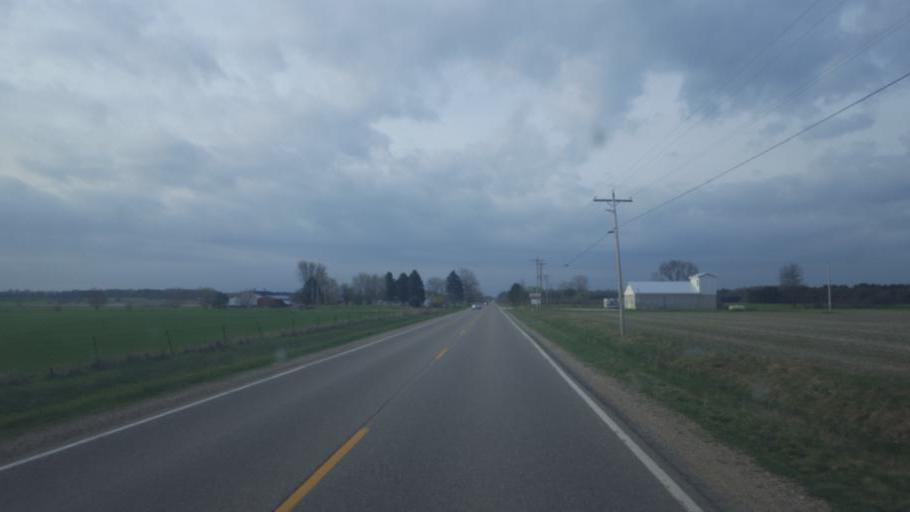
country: US
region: Michigan
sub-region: Isabella County
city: Lake Isabella
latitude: 43.5485
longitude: -84.9068
